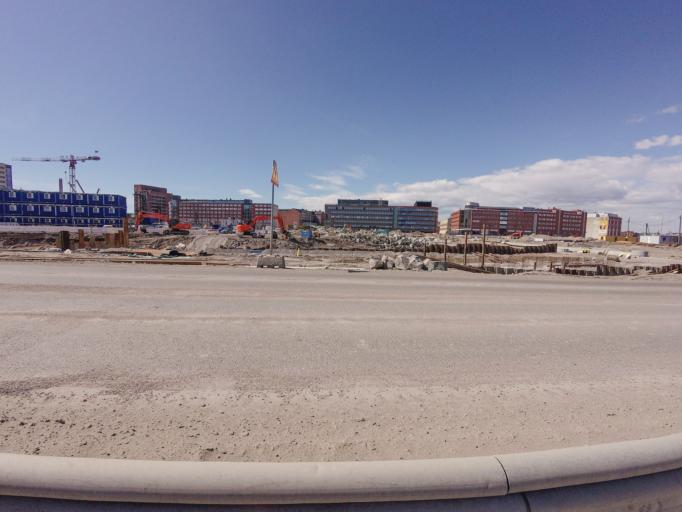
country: FI
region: Uusimaa
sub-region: Helsinki
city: Helsinki
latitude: 60.1894
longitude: 24.9823
